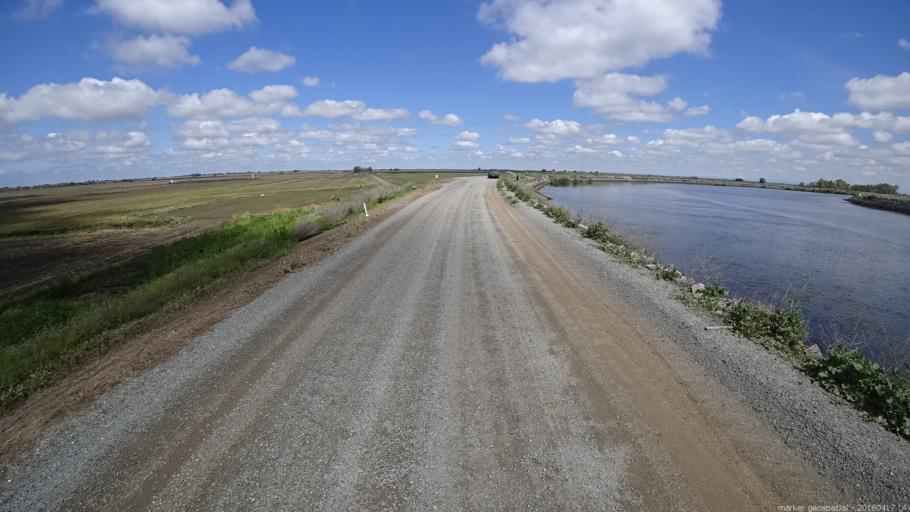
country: US
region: California
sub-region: Sacramento County
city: Walnut Grove
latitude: 38.1507
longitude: -121.5438
